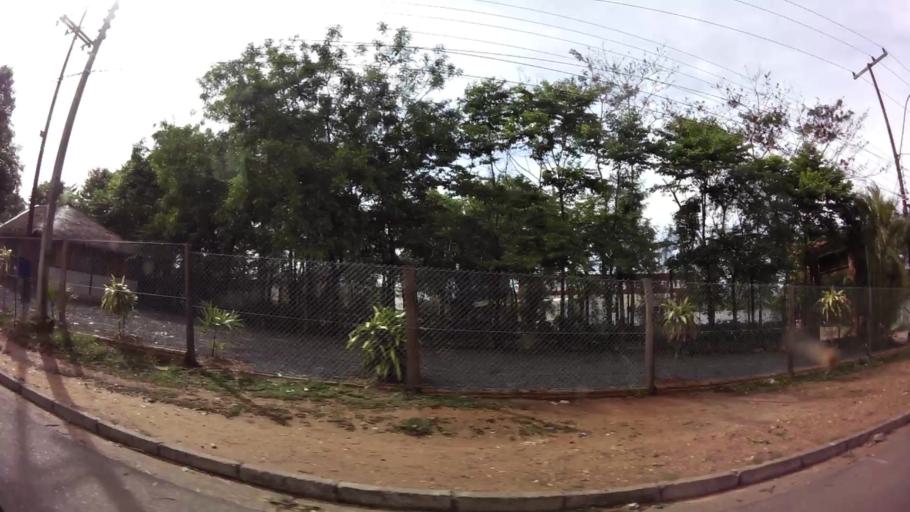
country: PY
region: Central
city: Limpio
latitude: -25.1659
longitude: -57.4685
